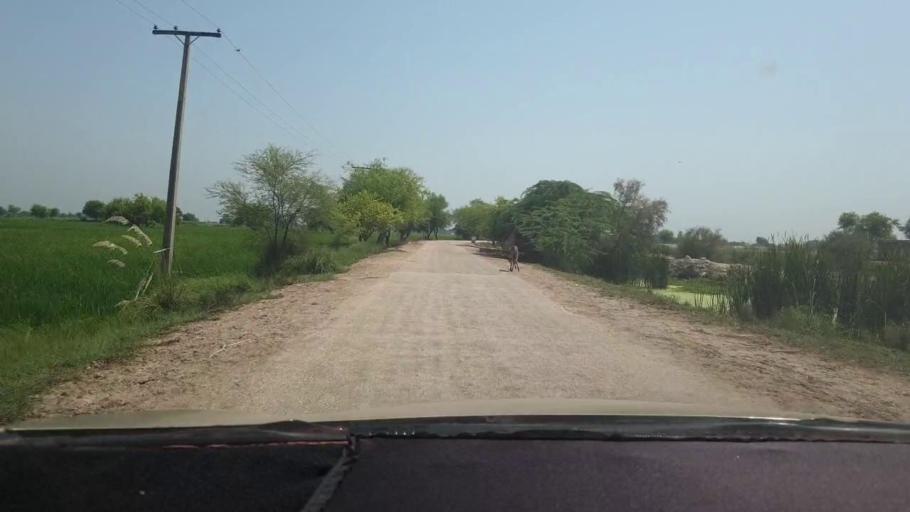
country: PK
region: Sindh
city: Miro Khan
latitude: 27.6813
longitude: 68.0956
